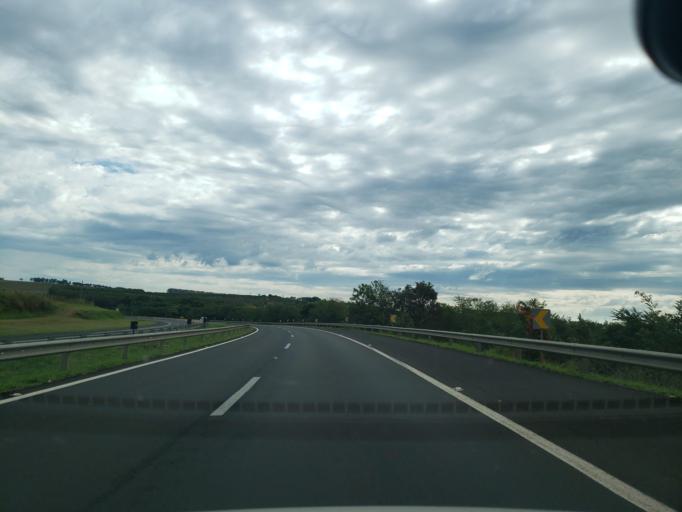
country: BR
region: Sao Paulo
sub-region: Bauru
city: Bauru
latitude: -22.1971
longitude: -49.1892
